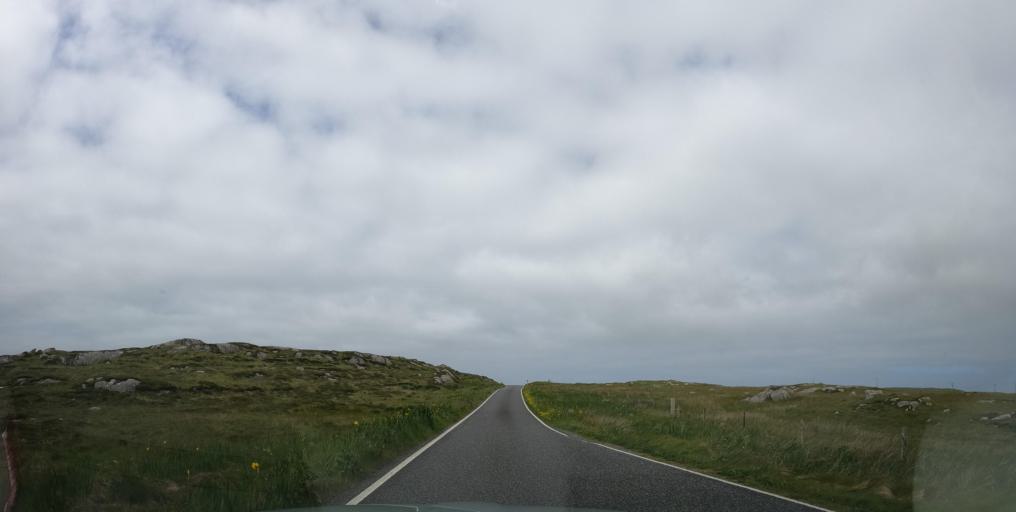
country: GB
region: Scotland
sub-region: Eilean Siar
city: Isle of South Uist
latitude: 57.1032
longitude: -7.3511
